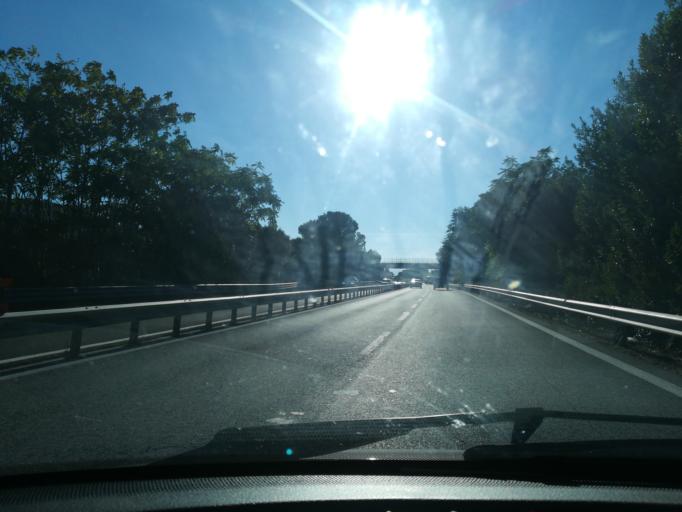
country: IT
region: The Marches
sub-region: Provincia di Macerata
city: Sforzacosta
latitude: 43.2558
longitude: 13.4519
